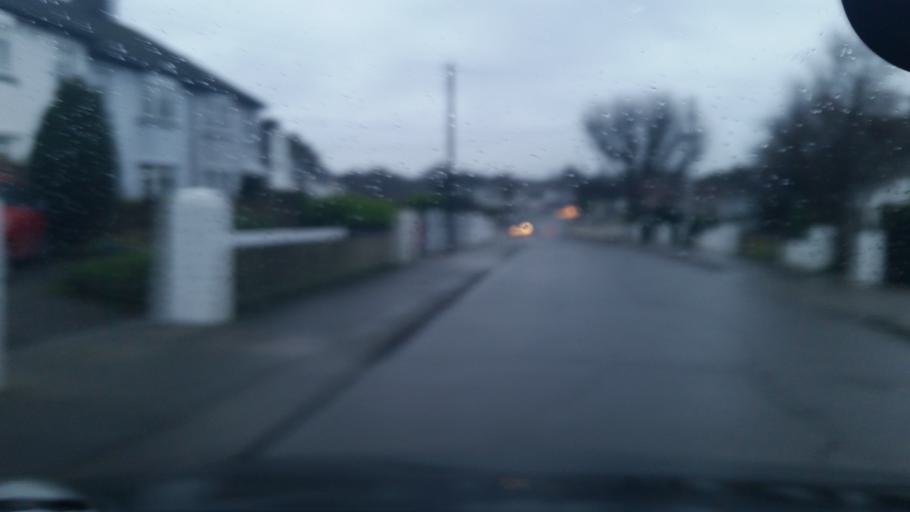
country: IE
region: Leinster
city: Marino
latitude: 53.3799
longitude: -6.2295
